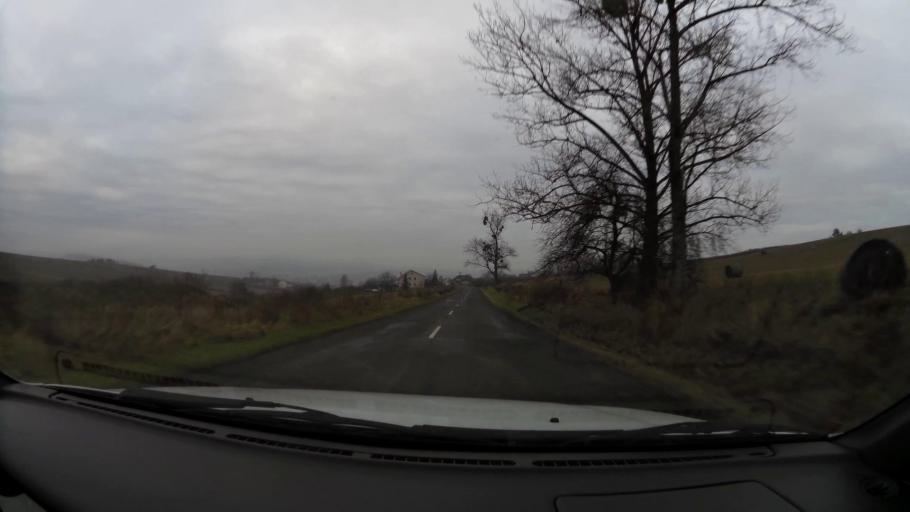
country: HU
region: Borsod-Abauj-Zemplen
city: Rudabanya
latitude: 48.3997
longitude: 20.6297
